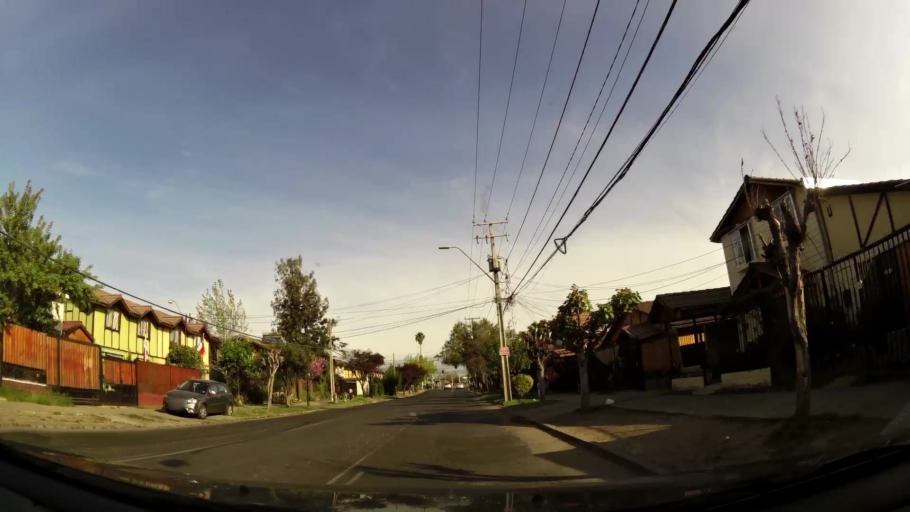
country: CL
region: Santiago Metropolitan
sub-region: Provincia de Cordillera
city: Puente Alto
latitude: -33.5791
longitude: -70.5695
